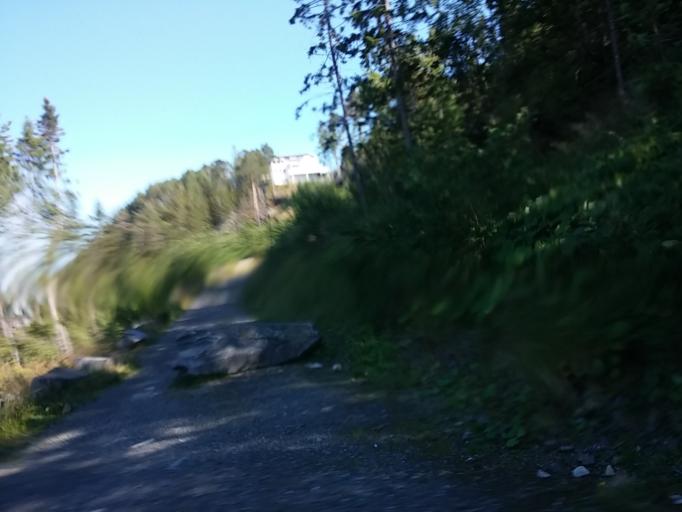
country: NO
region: Sor-Trondelag
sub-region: Malvik
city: Hommelvik
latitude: 63.4305
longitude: 10.7540
